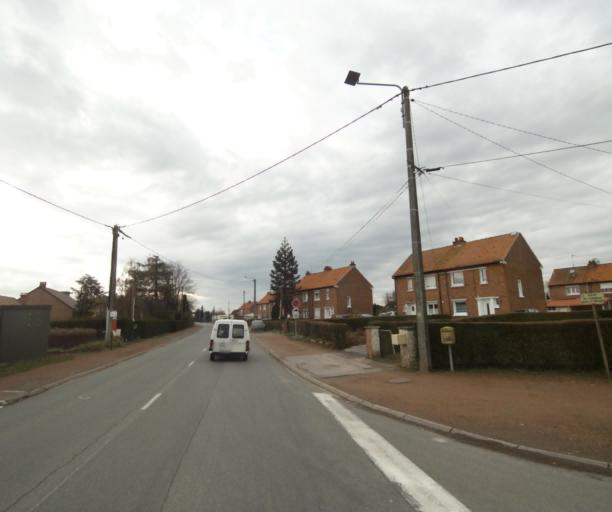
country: FR
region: Nord-Pas-de-Calais
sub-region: Departement du Nord
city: Sebourg
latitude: 50.3514
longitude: 3.6383
